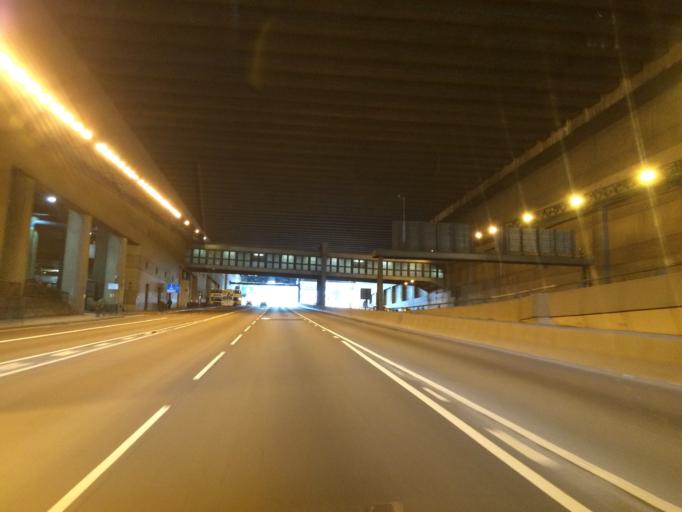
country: HK
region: Kowloon City
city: Kowloon
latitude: 22.3075
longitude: 114.2327
